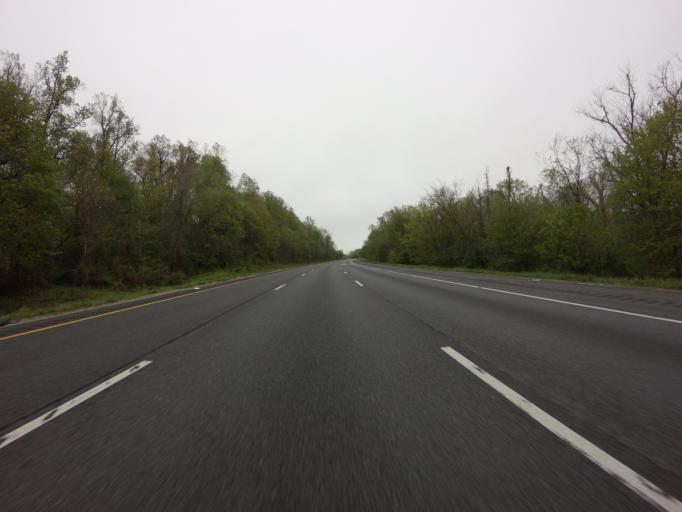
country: US
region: Maryland
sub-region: Washington County
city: Boonsboro
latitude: 39.5559
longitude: -77.6123
